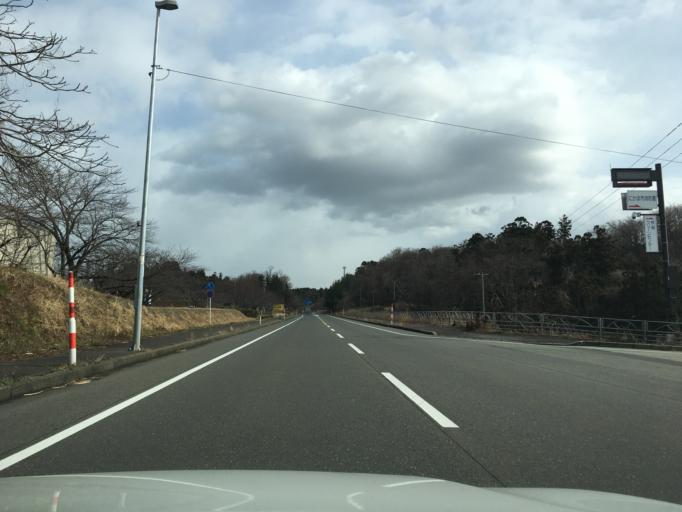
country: JP
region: Yamagata
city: Yuza
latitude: 39.2471
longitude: 139.9235
